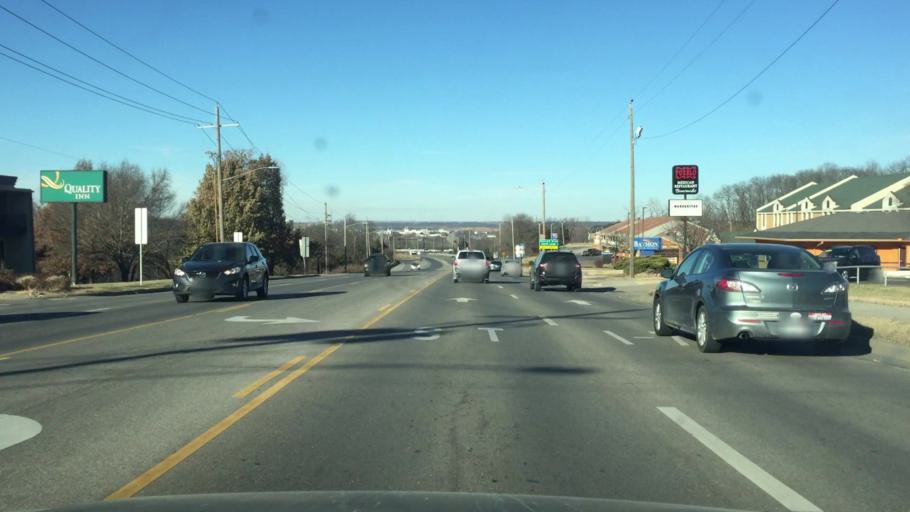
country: US
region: Kansas
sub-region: Douglas County
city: Lawrence
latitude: 38.9685
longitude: -95.2604
